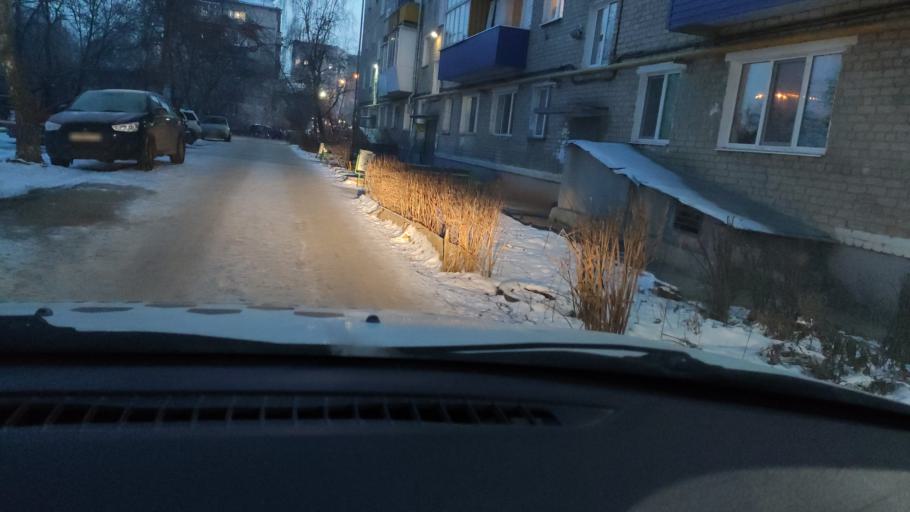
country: RU
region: Perm
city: Kungur
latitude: 57.4376
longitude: 56.9338
